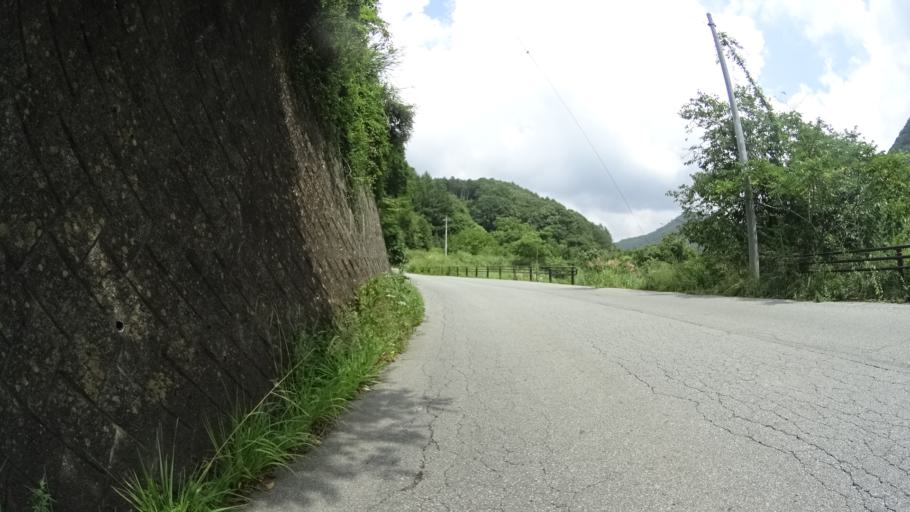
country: JP
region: Yamanashi
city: Nirasaki
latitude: 35.8920
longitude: 138.5351
